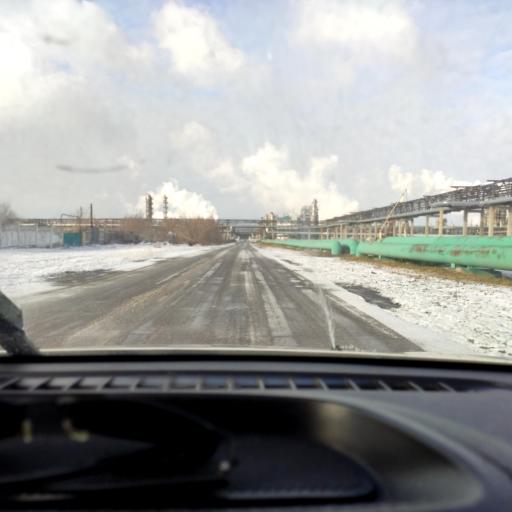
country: RU
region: Samara
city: Tol'yatti
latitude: 53.5360
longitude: 49.4721
